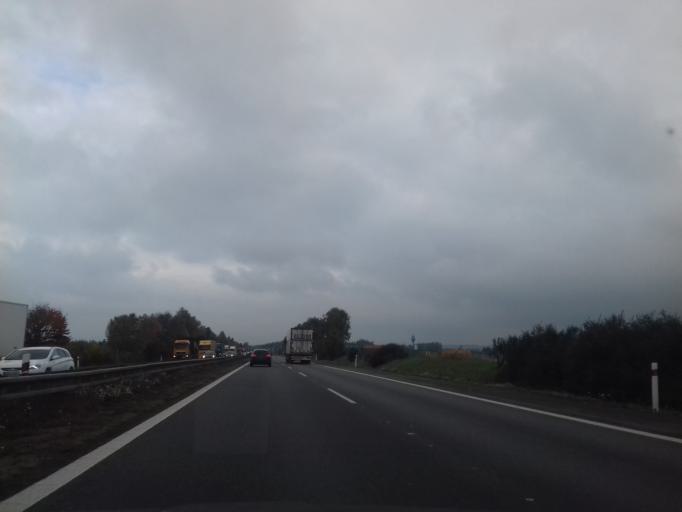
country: CZ
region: Central Bohemia
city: Zruc nad Sazavou
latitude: 49.6683
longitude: 15.1184
